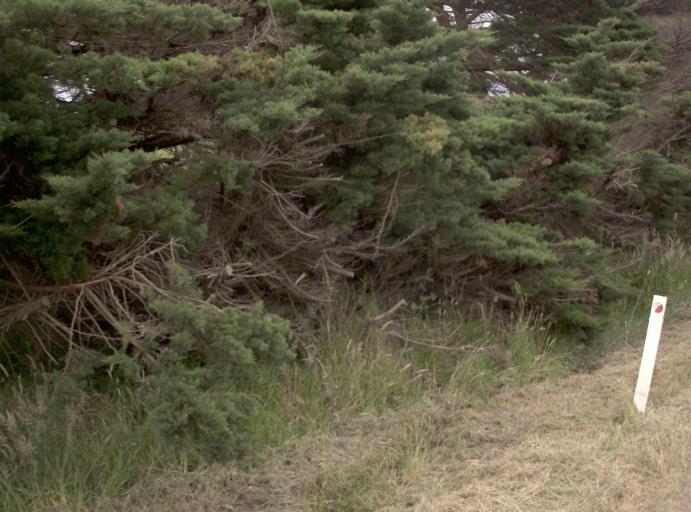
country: AU
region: Victoria
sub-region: Bass Coast
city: North Wonthaggi
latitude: -38.5809
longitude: 145.6278
